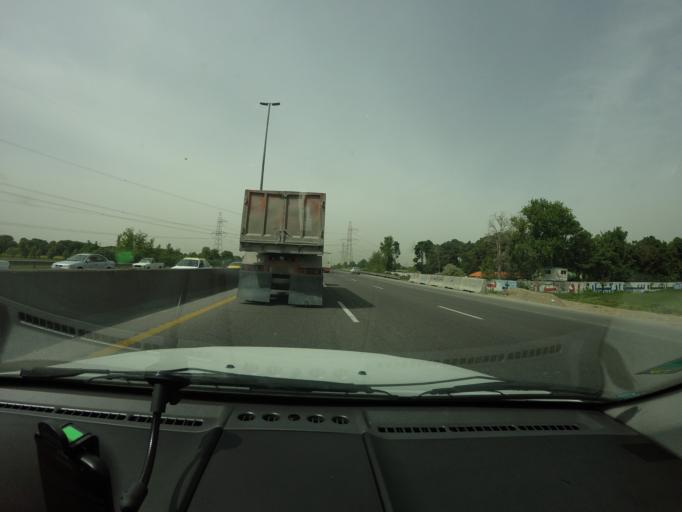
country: IR
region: Tehran
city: Eslamshahr
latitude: 35.6198
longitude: 51.2230
